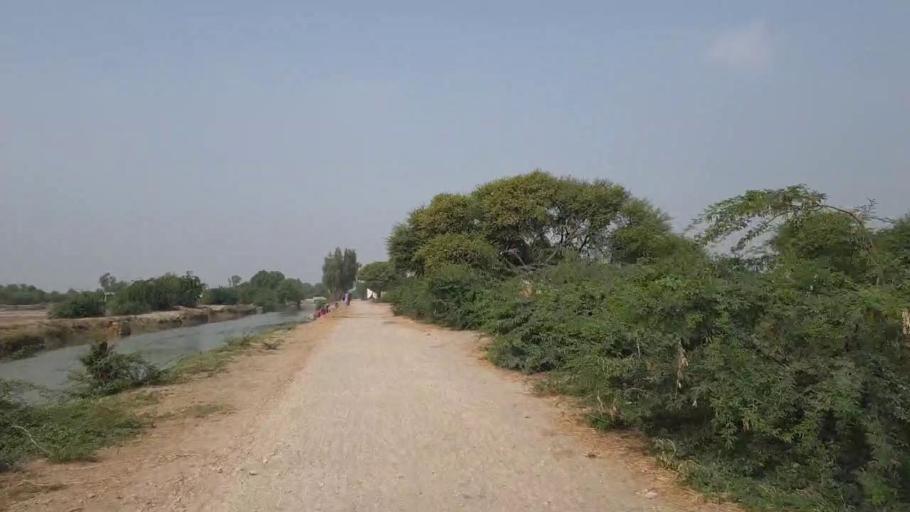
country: PK
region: Sindh
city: Kario
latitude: 24.8764
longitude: 68.5152
